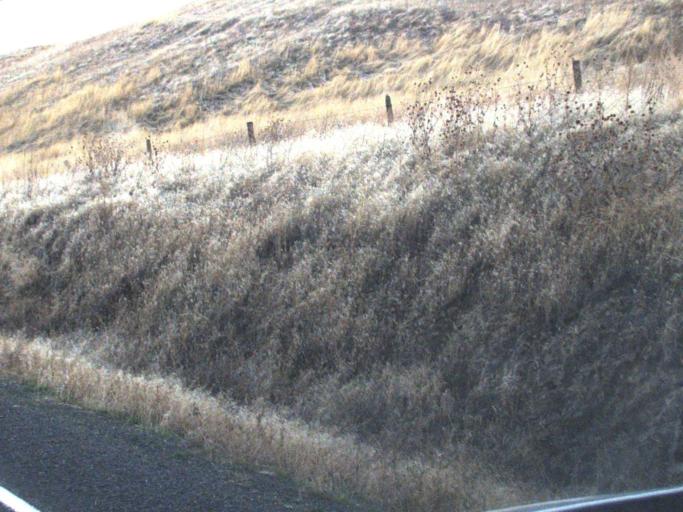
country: US
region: Washington
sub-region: Columbia County
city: Dayton
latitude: 46.4617
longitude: -117.9612
